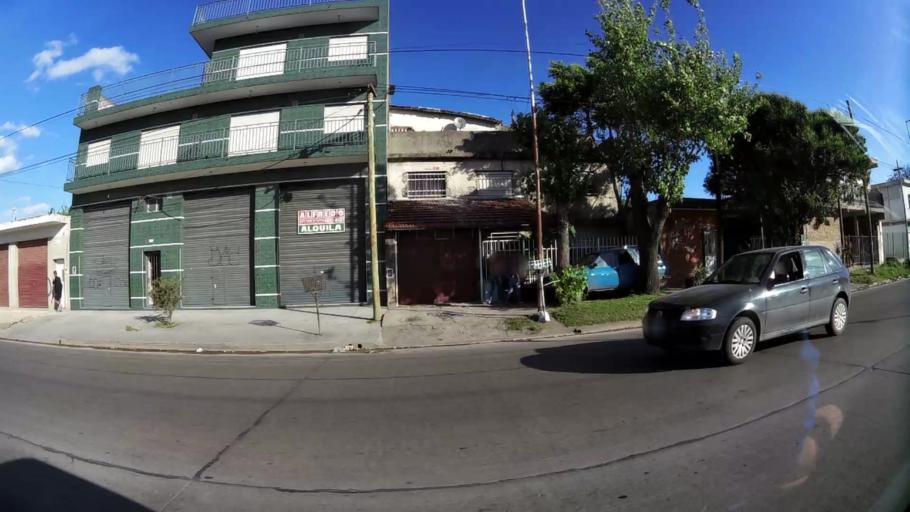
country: AR
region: Buenos Aires
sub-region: Partido de Moron
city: Moron
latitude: -34.6859
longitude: -58.6222
